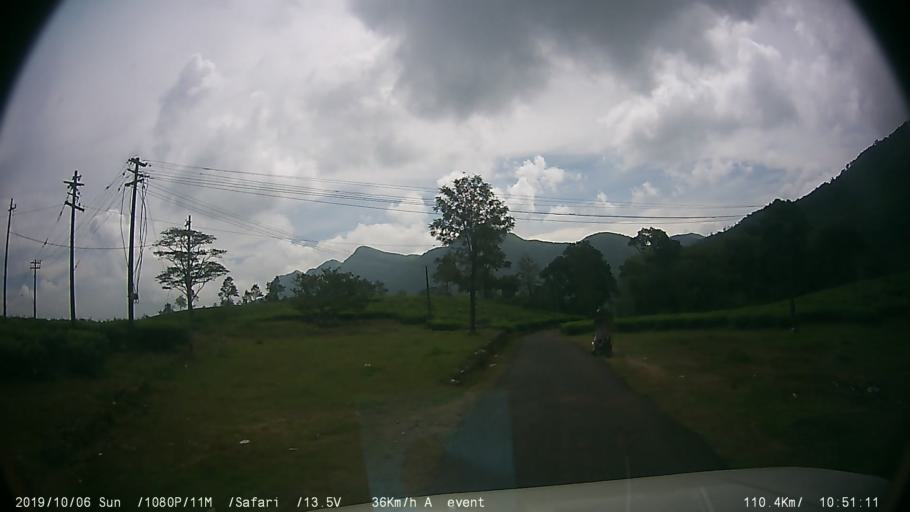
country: IN
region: Kerala
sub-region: Kottayam
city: Erattupetta
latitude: 9.6194
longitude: 76.9568
